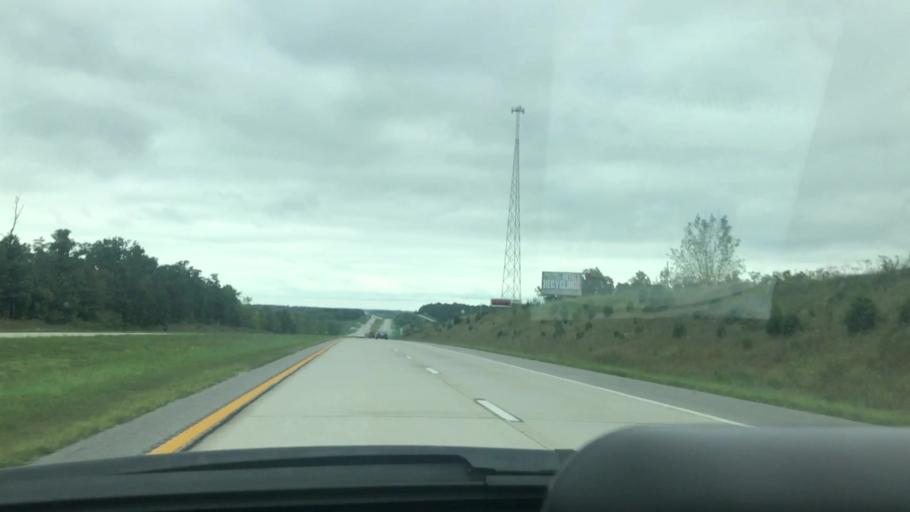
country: US
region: Missouri
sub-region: Greene County
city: Fair Grove
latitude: 37.5073
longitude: -93.1388
